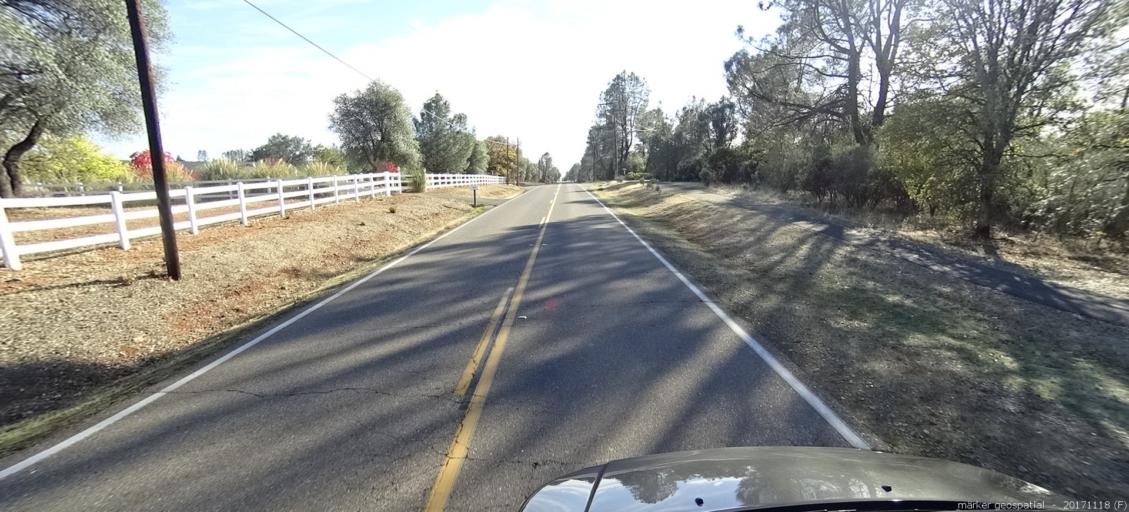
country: US
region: California
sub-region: Shasta County
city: Redding
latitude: 40.4659
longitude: -122.4546
